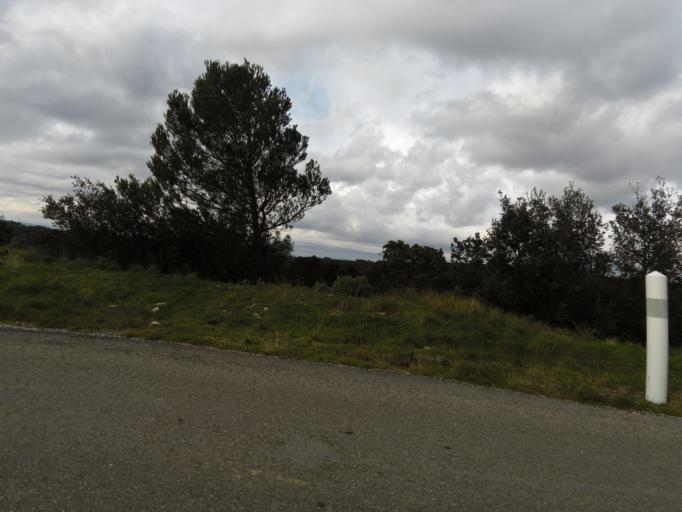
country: FR
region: Languedoc-Roussillon
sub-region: Departement du Gard
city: Clarensac
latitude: 43.8354
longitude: 4.1864
